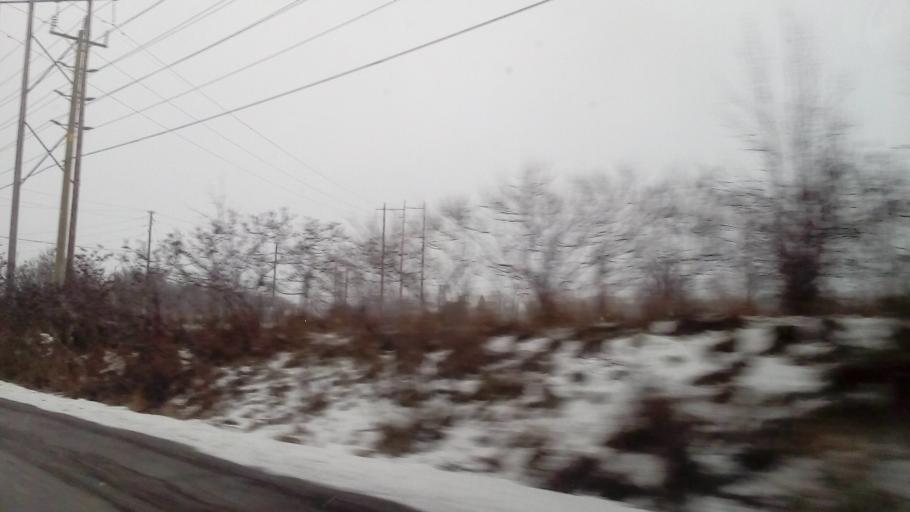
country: CA
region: Quebec
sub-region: Outaouais
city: Gatineau
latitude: 45.4524
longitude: -75.5749
